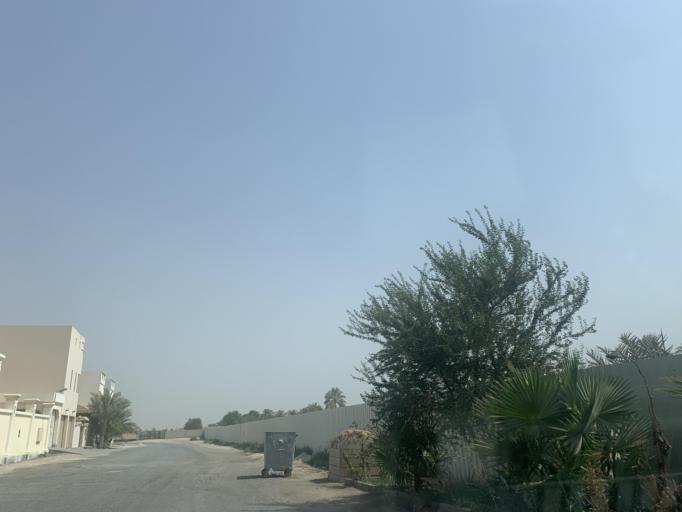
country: BH
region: Northern
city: Madinat `Isa
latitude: 26.1872
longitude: 50.4928
